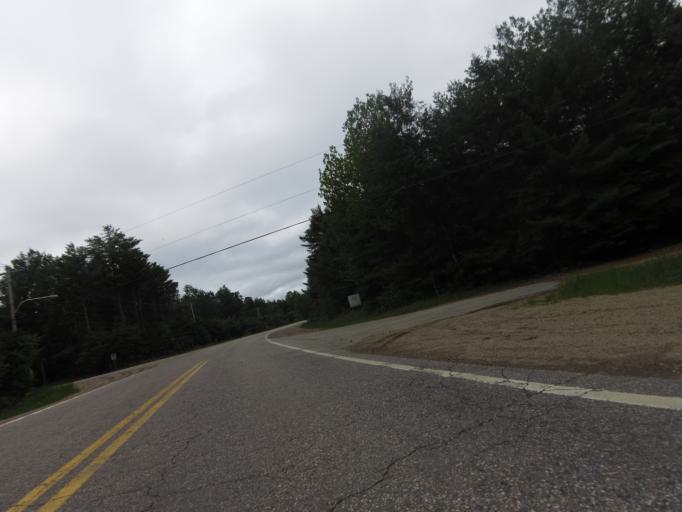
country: CA
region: Quebec
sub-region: Outaouais
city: Shawville
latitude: 45.8585
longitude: -76.4118
